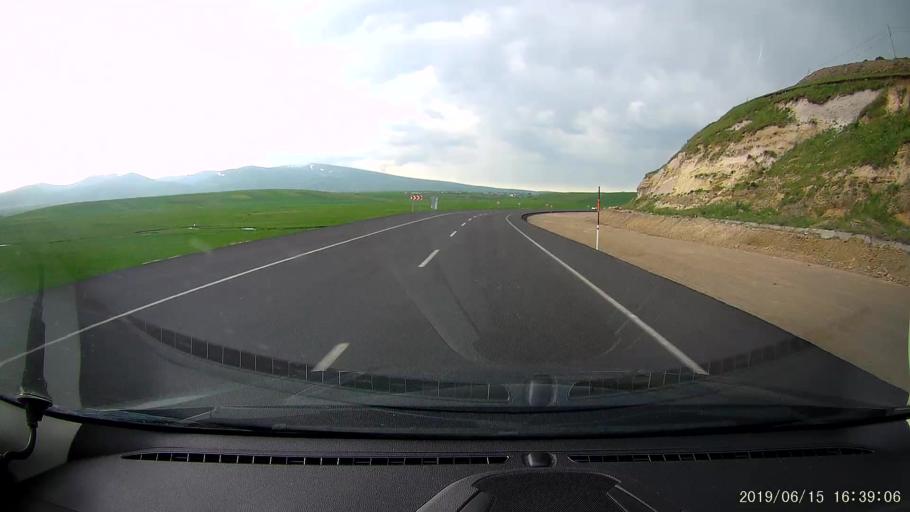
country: TR
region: Ardahan
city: Haskoy
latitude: 40.9863
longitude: 42.8940
